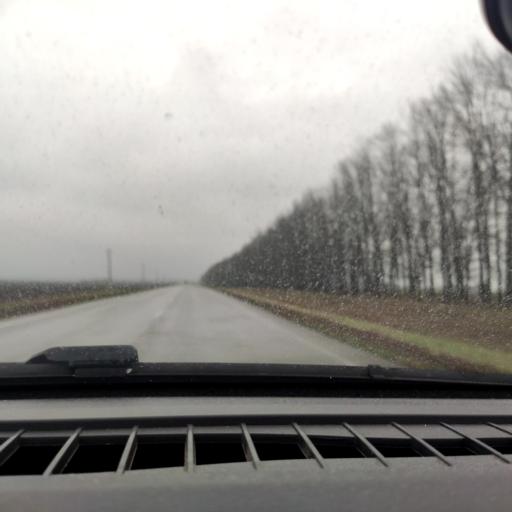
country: RU
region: Belgorod
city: Ilovka
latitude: 50.7451
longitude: 38.7115
